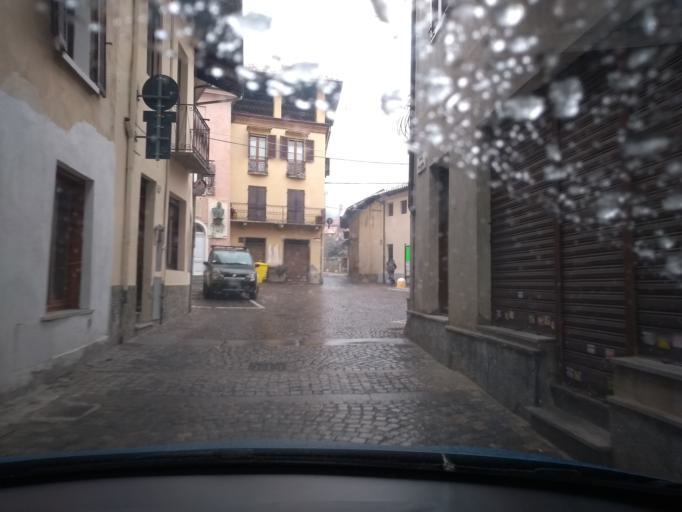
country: IT
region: Piedmont
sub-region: Provincia di Torino
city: Balangero
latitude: 45.2754
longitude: 7.5202
